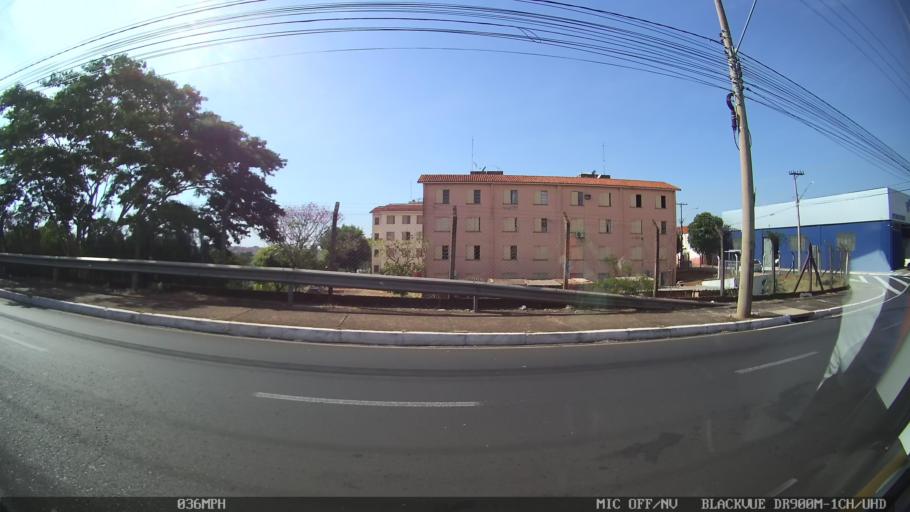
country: BR
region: Sao Paulo
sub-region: Sao Jose Do Rio Preto
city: Sao Jose do Rio Preto
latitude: -20.7999
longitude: -49.3970
